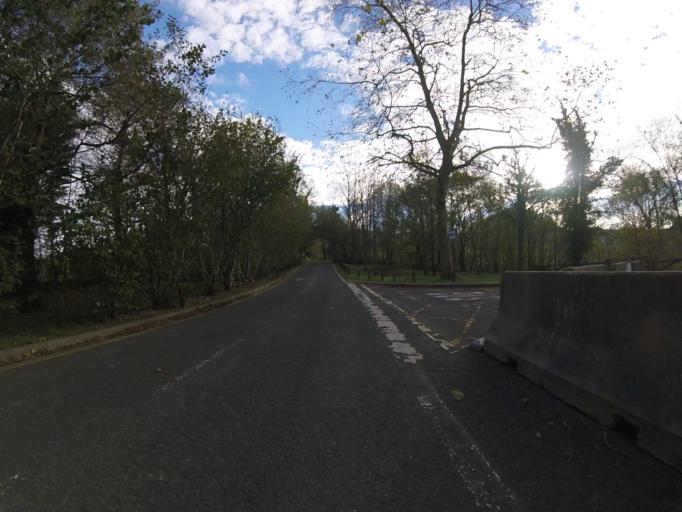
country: ES
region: Basque Country
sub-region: Provincia de Guipuzcoa
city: Errenteria
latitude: 43.2675
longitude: -1.9004
